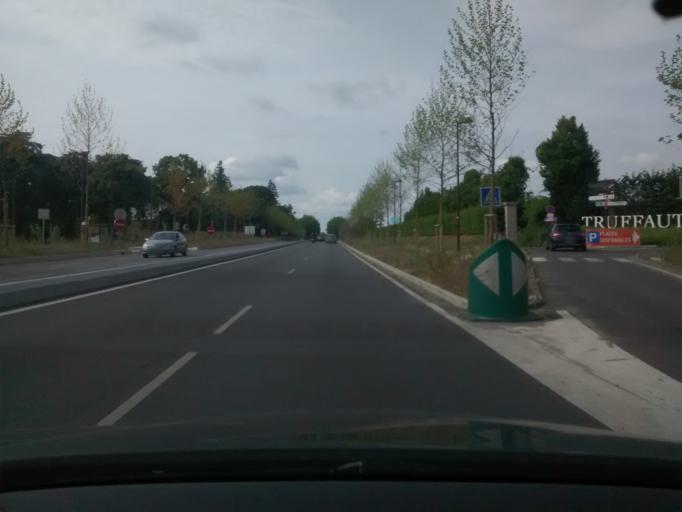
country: FR
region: Ile-de-France
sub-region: Departement des Yvelines
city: Le Chesnay
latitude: 48.8250
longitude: 2.1144
